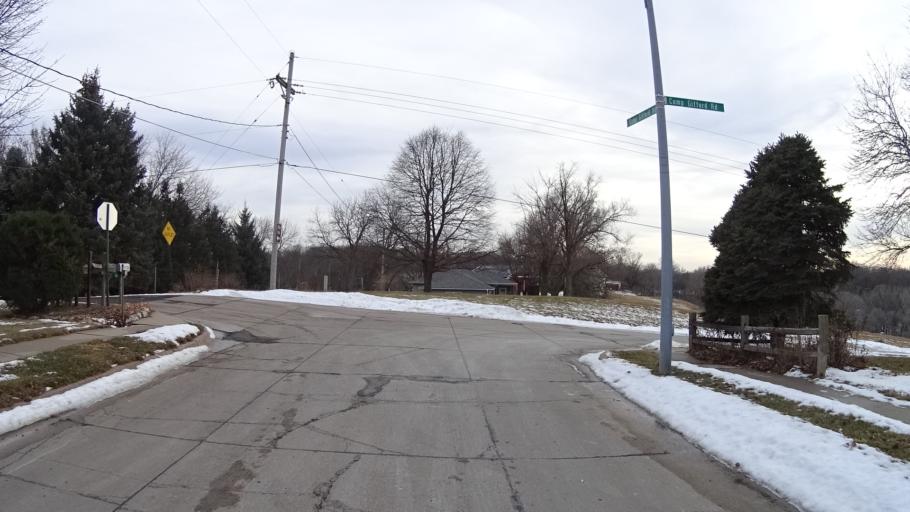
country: US
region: Nebraska
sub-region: Sarpy County
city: Bellevue
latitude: 41.1731
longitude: -95.9111
